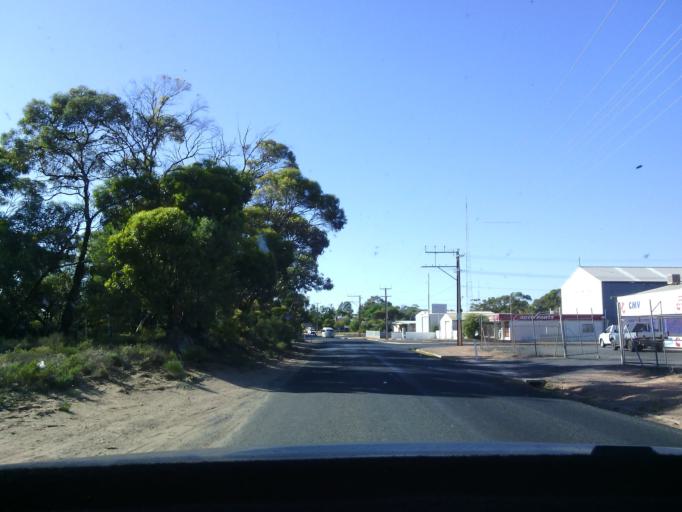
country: AU
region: South Australia
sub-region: Berri and Barmera
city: Berri
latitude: -34.2699
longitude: 140.6043
